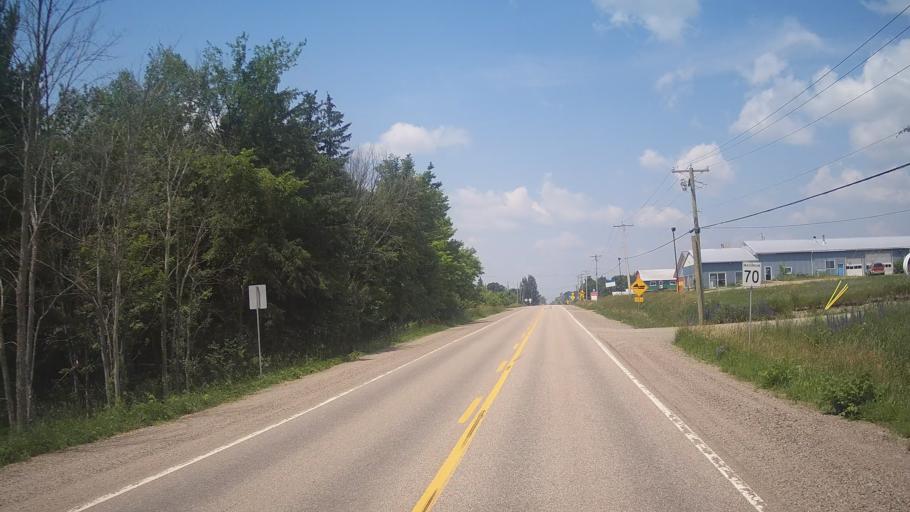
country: CA
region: Quebec
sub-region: Outaouais
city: Shawville
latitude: 45.5959
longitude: -76.4836
